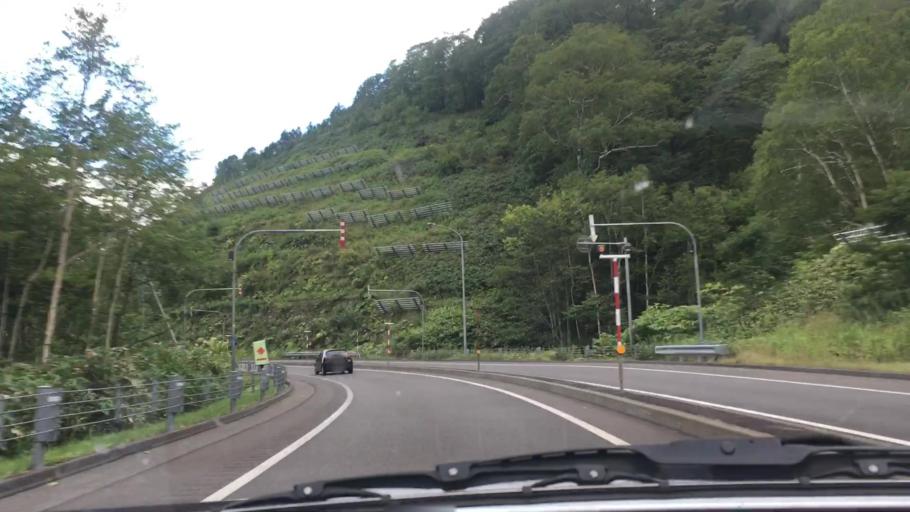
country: JP
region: Hokkaido
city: Shimo-furano
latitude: 43.1501
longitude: 142.7734
